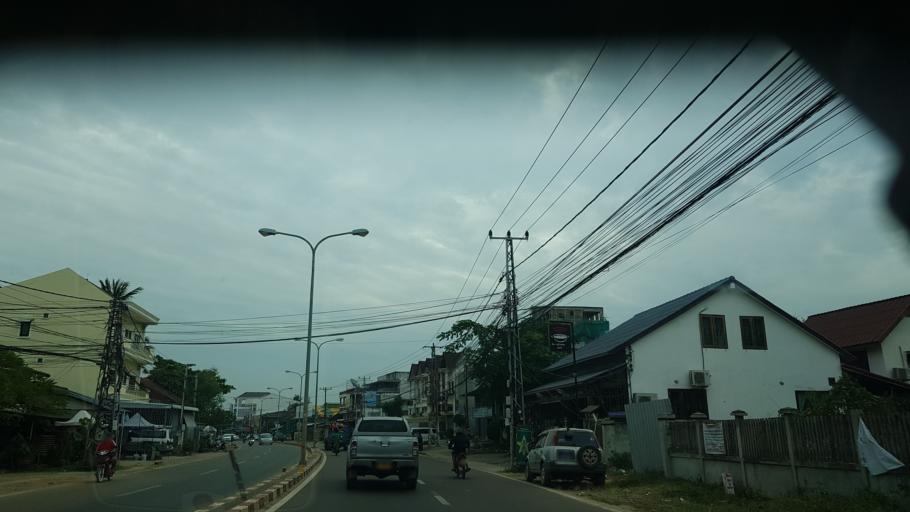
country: TH
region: Nong Khai
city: Si Chiang Mai
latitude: 17.9273
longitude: 102.6164
